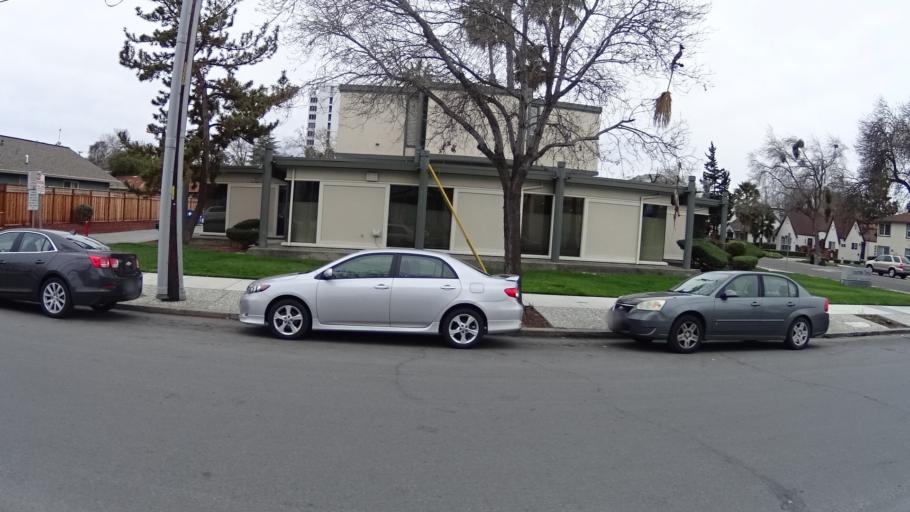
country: US
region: California
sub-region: Santa Clara County
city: San Jose
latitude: 37.3498
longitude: -121.8979
